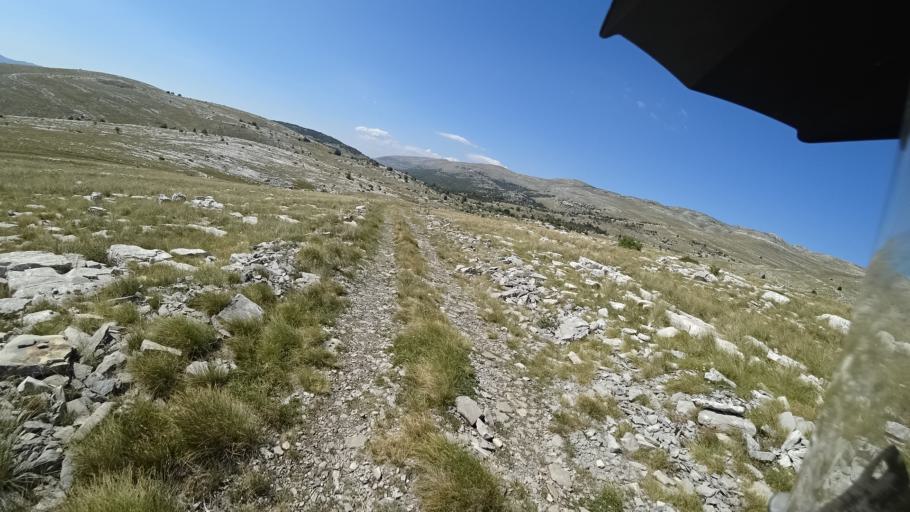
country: HR
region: Splitsko-Dalmatinska
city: Hrvace
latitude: 43.9001
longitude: 16.5971
